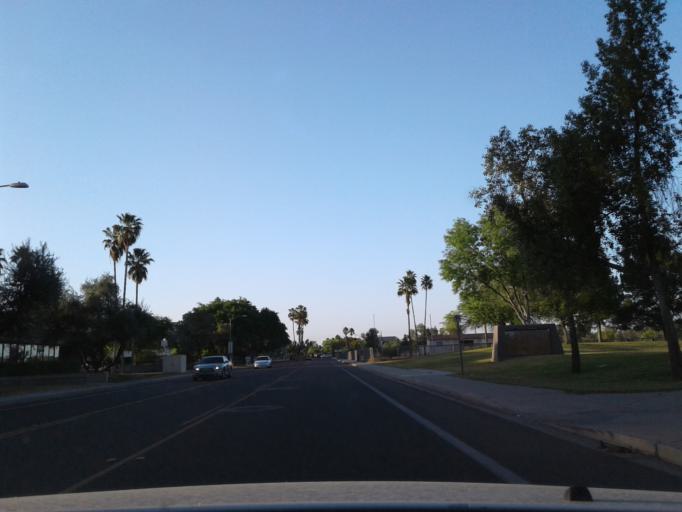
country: US
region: Arizona
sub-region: Maricopa County
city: Glendale
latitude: 33.5791
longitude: -112.1134
